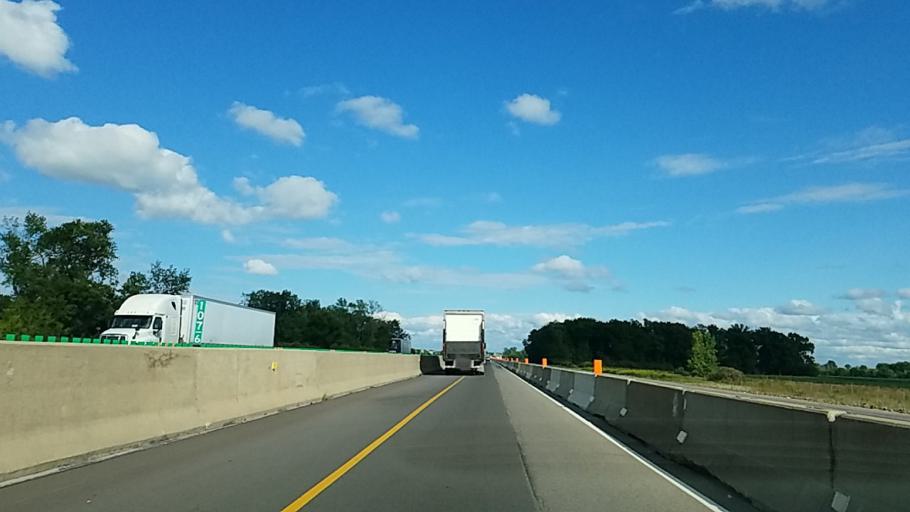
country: US
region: Ohio
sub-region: Huron County
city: Bellevue
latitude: 41.3478
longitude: -82.8161
